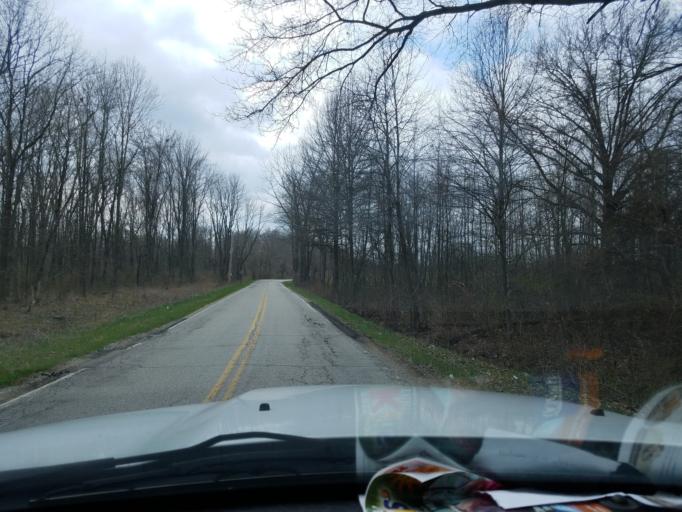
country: US
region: Indiana
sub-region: Vigo County
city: Terre Haute
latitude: 39.4138
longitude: -87.3443
